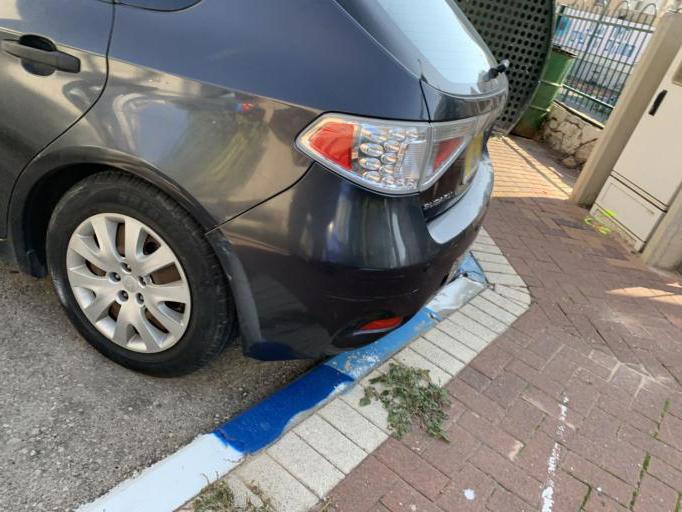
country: IL
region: Tel Aviv
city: Ramat Gan
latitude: 32.0887
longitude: 34.8033
